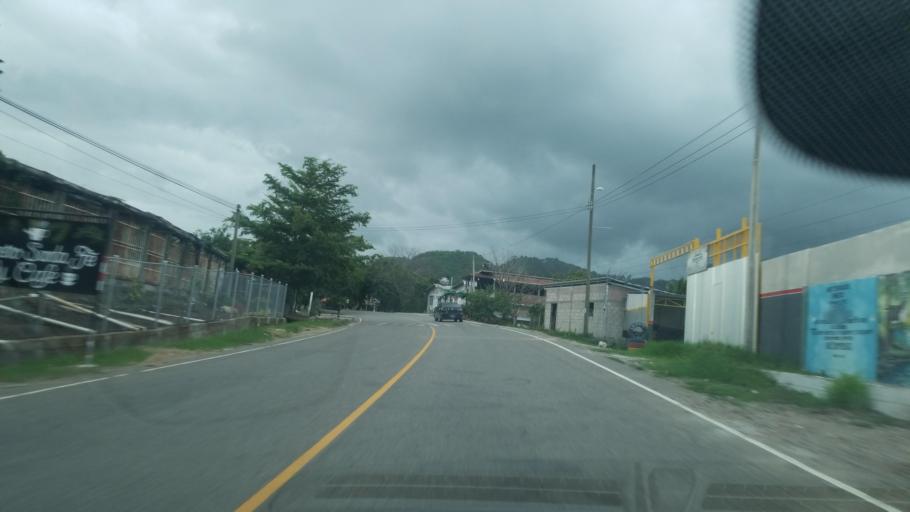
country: HN
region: Ocotepeque
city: Sinuapa
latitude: 14.5075
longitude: -89.2277
